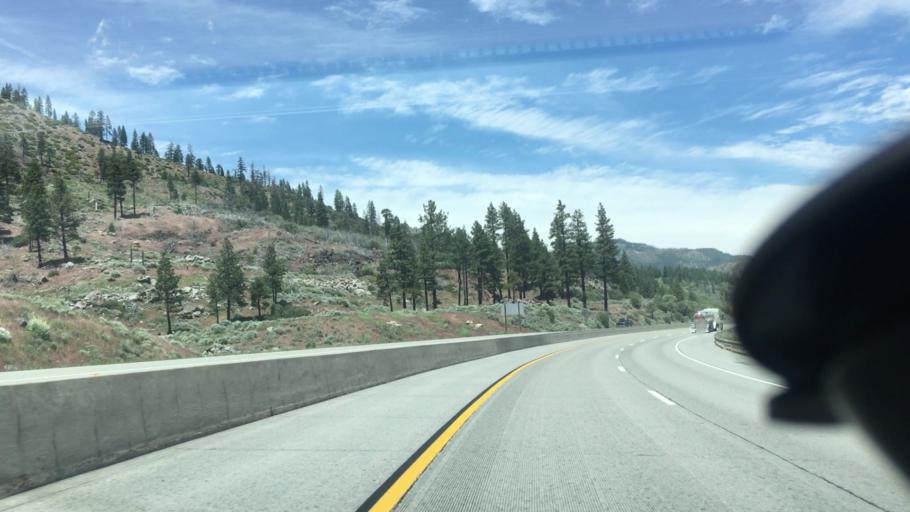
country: US
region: Nevada
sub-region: Washoe County
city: Verdi
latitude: 39.3857
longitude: -120.0248
